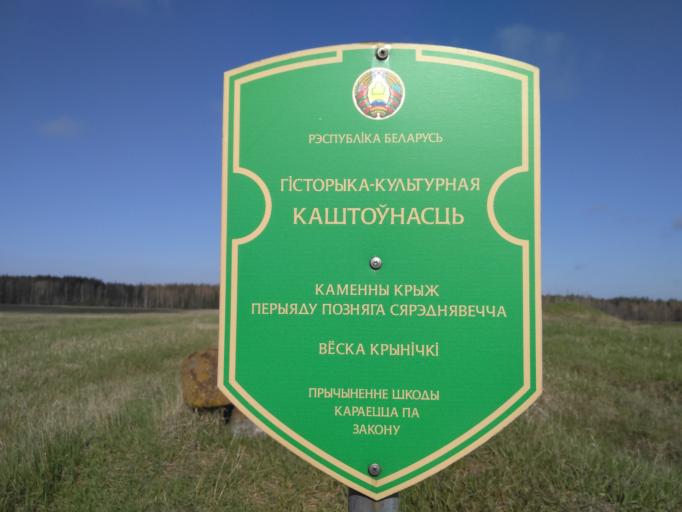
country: BY
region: Minsk
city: Loshnitsa
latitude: 54.4351
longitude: 28.7070
